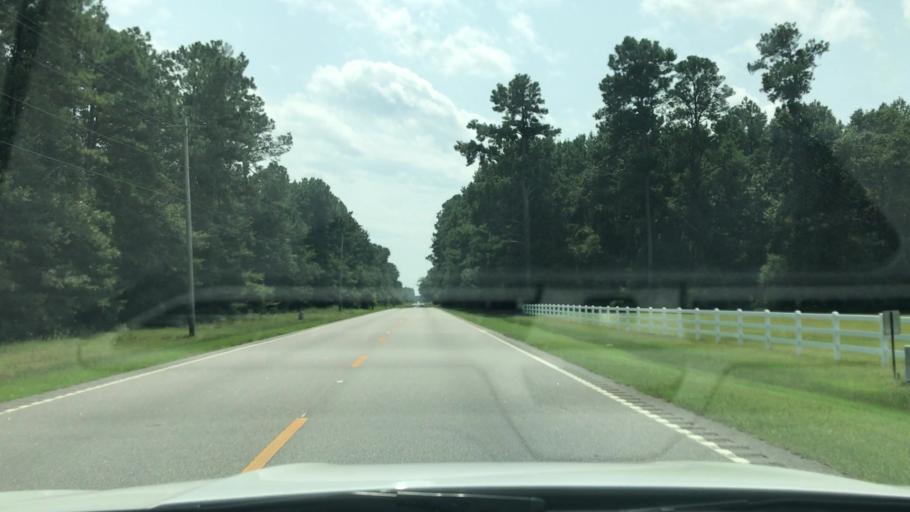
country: US
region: South Carolina
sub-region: Horry County
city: Conway
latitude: 33.7437
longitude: -79.0797
